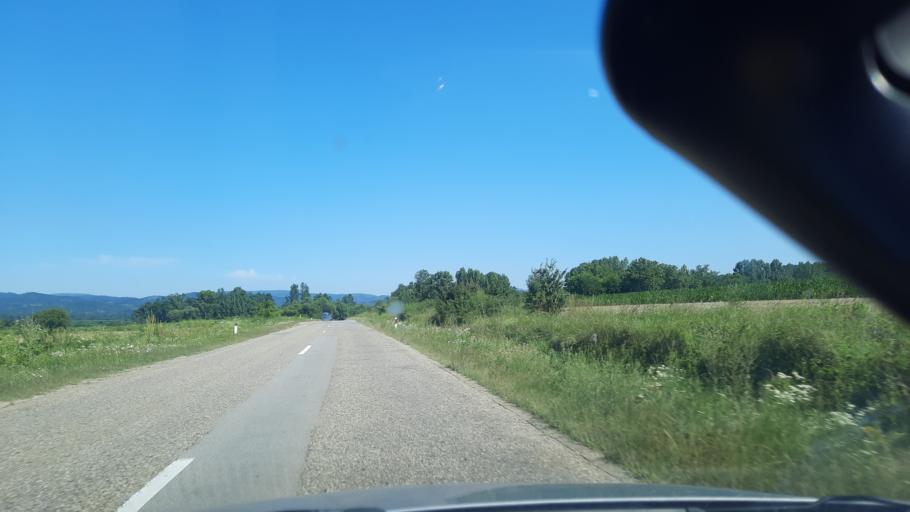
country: RS
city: Turija
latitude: 44.5645
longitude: 21.5280
